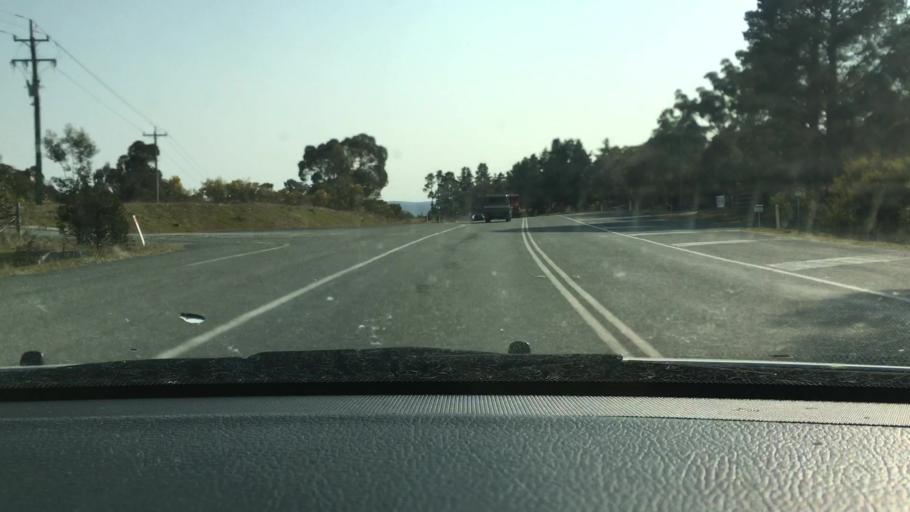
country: AU
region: New South Wales
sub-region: Queanbeyan
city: Queanbeyan
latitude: -35.4036
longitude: 149.2298
